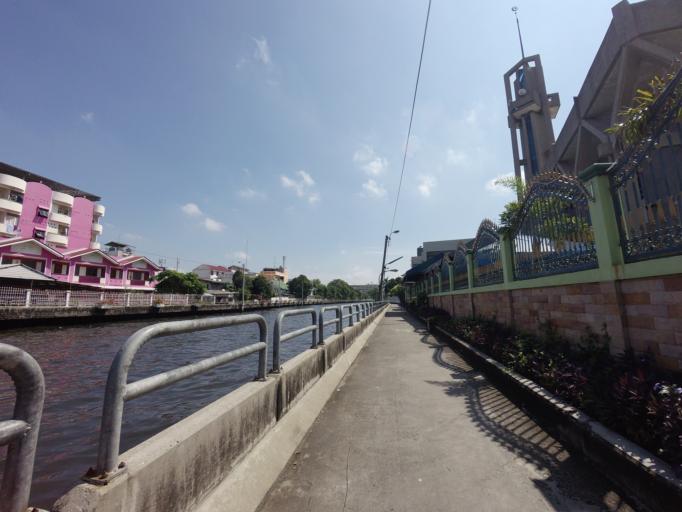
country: TH
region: Bangkok
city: Wang Thonglang
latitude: 13.7617
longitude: 100.6197
